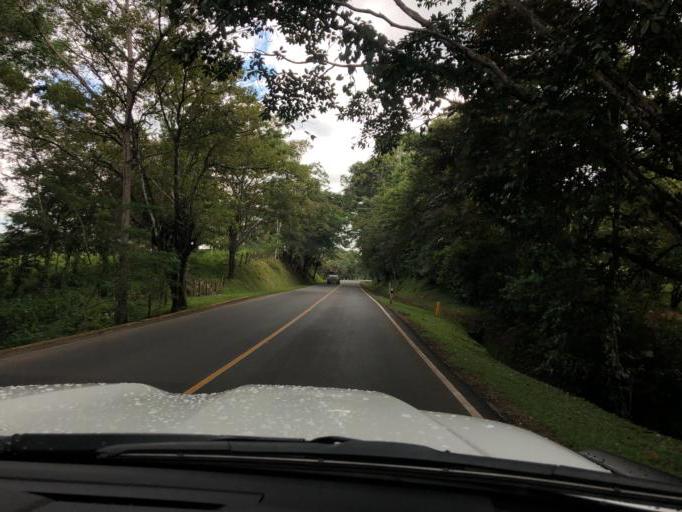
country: NI
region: Chontales
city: Villa Sandino
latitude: 11.9976
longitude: -84.8824
